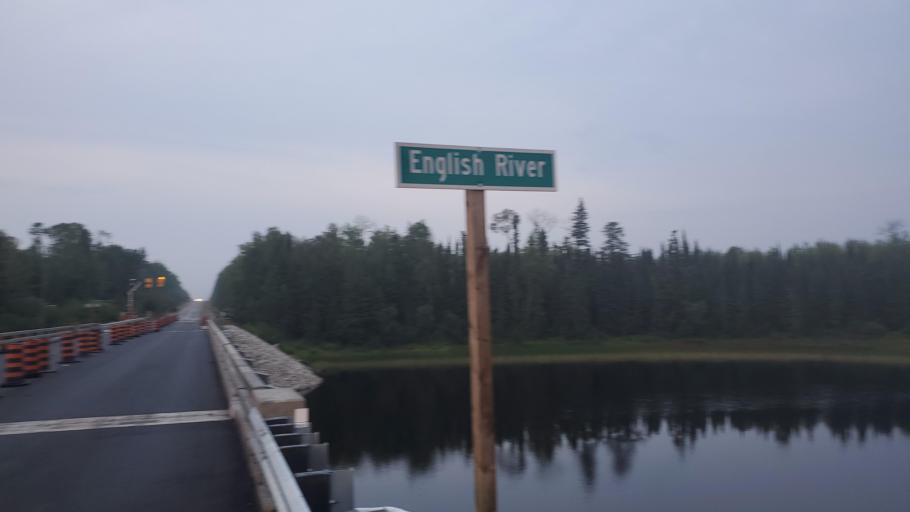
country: CA
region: Ontario
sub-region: Rainy River District
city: Atikokan
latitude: 49.6076
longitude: -91.3701
